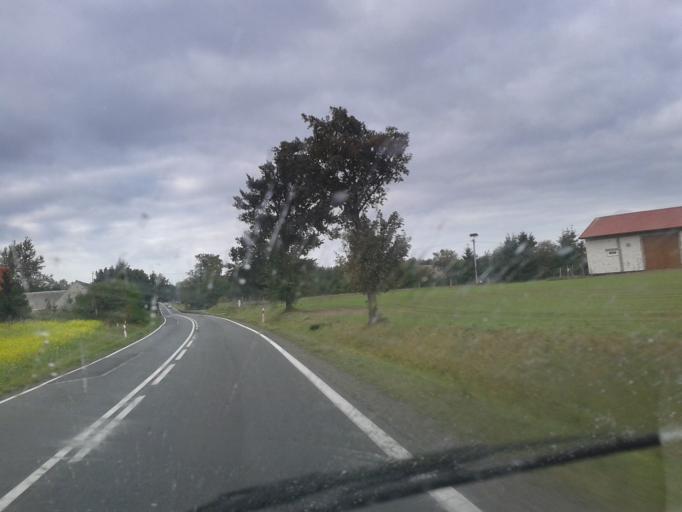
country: PL
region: Kujawsko-Pomorskie
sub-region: Powiat sepolenski
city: Sepolno Krajenskie
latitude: 53.4849
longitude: 17.5191
